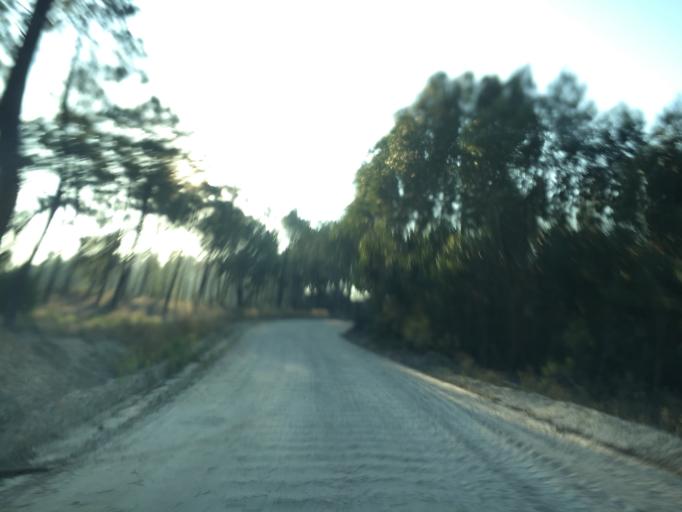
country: PT
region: Portalegre
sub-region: Ponte de Sor
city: Santo Andre
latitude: 39.0916
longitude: -8.3658
